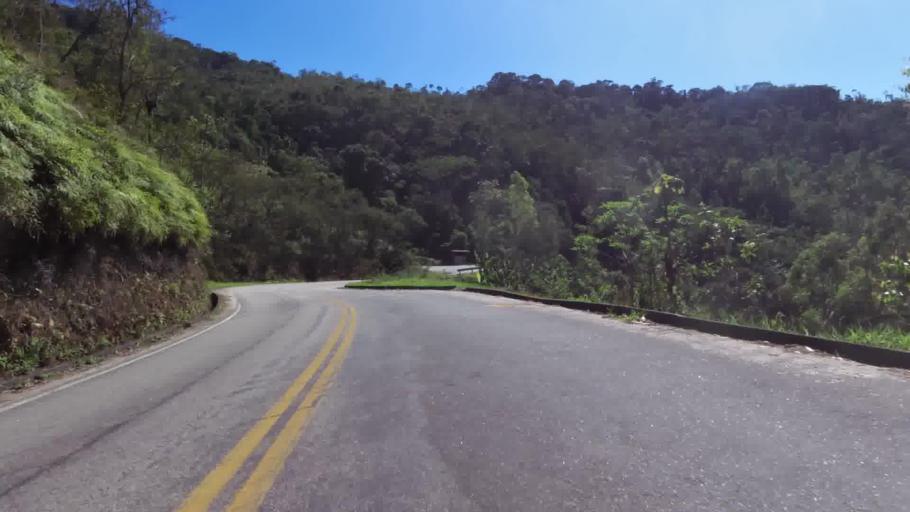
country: BR
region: Espirito Santo
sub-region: Vargem Alta
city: Vargem Alta
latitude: -20.6920
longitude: -40.9316
